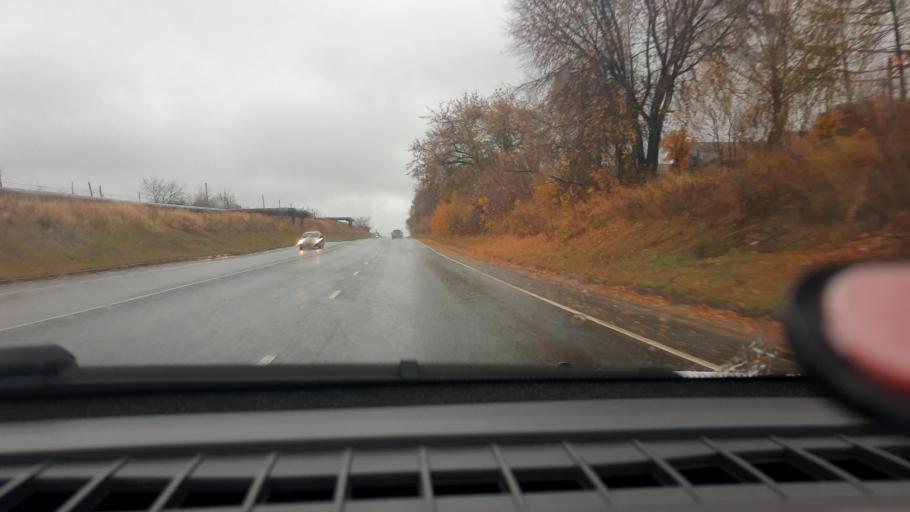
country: RU
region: Nizjnij Novgorod
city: Kstovo
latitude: 56.1323
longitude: 44.1773
